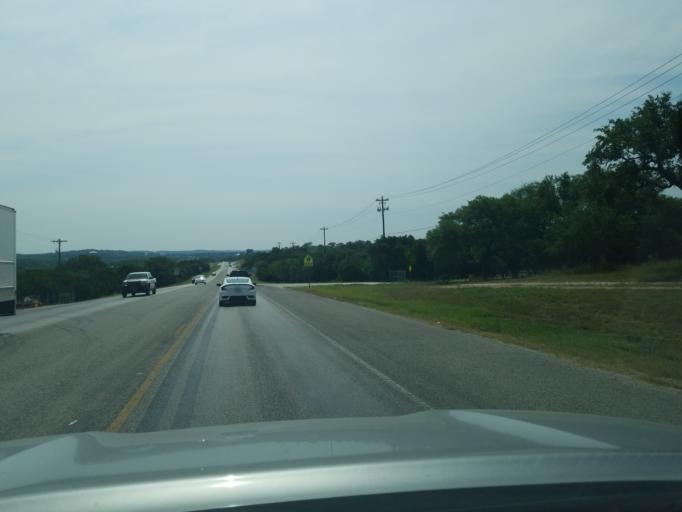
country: US
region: Texas
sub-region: Comal County
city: Bulverde
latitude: 29.7997
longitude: -98.4373
